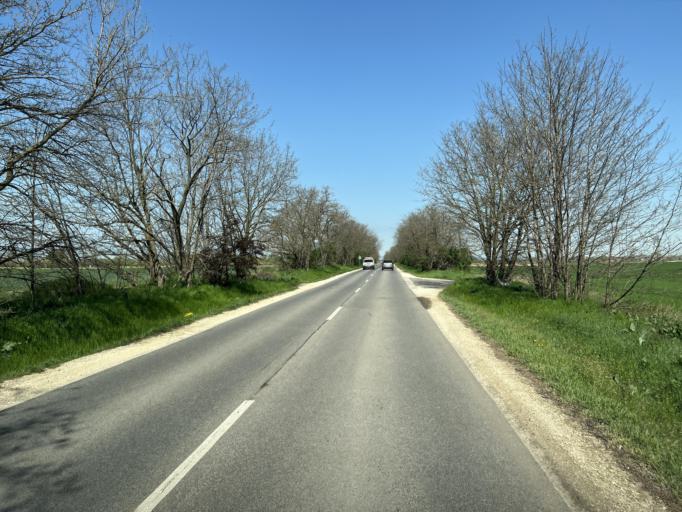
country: HU
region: Pest
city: Ocsa
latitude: 47.3100
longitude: 19.2100
